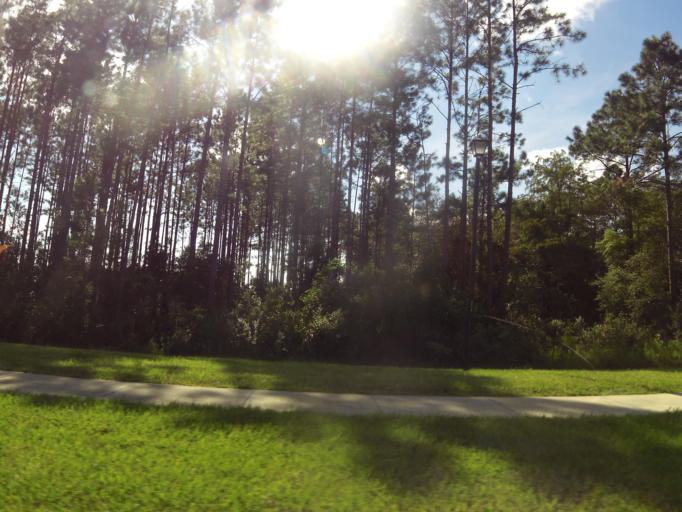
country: US
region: Florida
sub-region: Saint Johns County
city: Palm Valley
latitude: 30.0780
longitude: -81.4682
